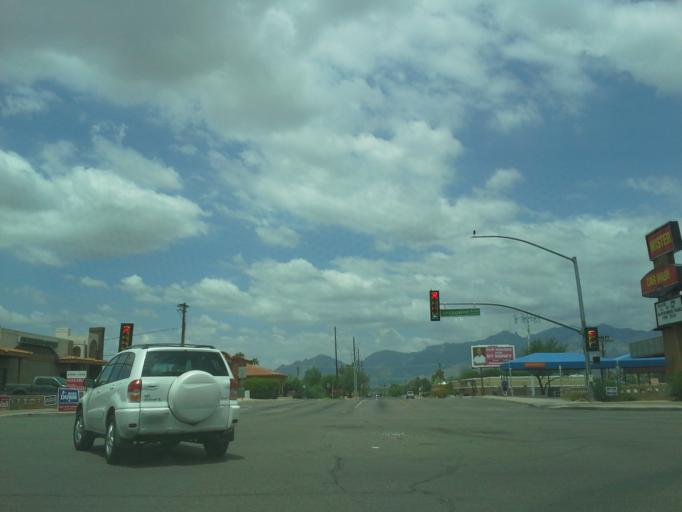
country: US
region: Arizona
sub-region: Pima County
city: Tucson
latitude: 32.2359
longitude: -110.9267
